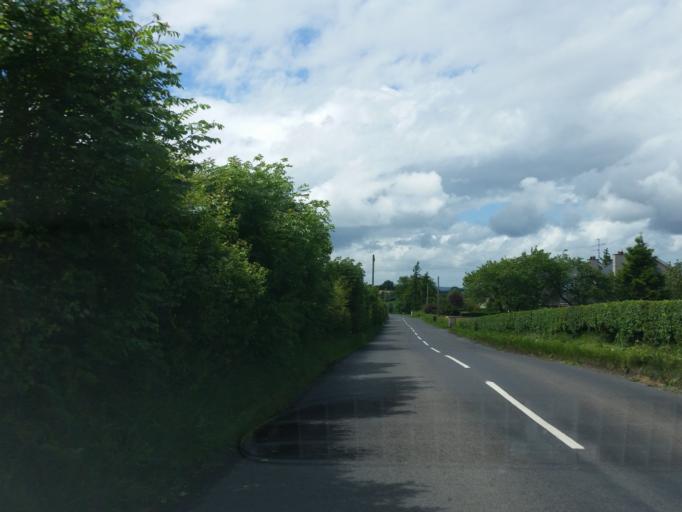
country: GB
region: Northern Ireland
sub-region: Omagh District
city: Omagh
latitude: 54.5543
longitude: -7.1493
